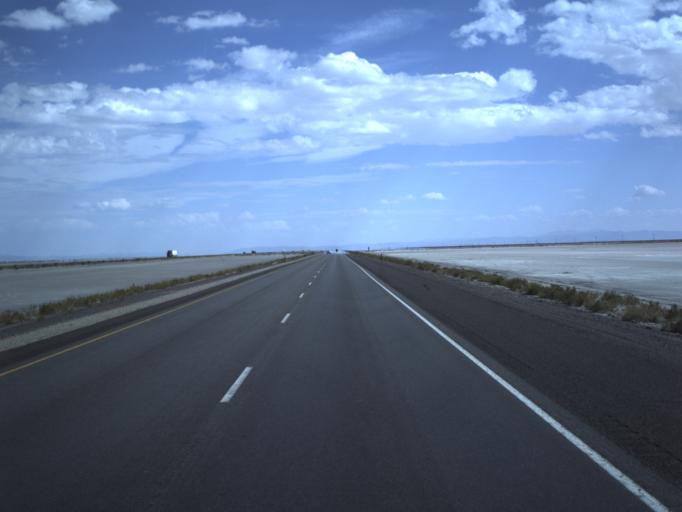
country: US
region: Utah
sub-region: Tooele County
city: Wendover
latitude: 40.7363
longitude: -113.7446
